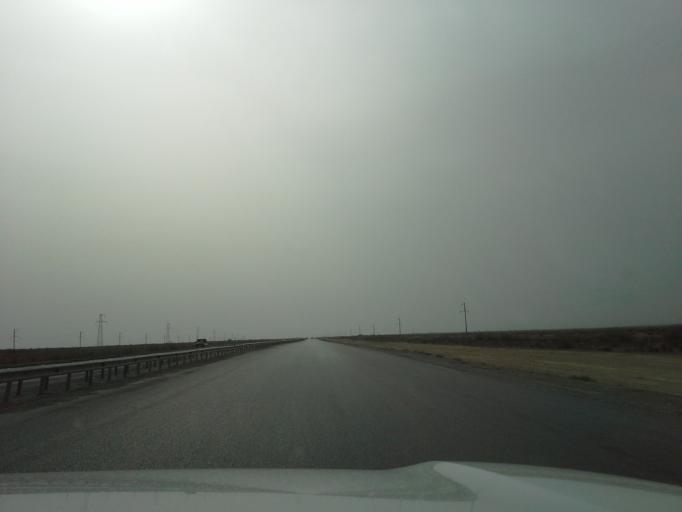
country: TM
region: Ahal
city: Kaka
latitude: 37.5101
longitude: 59.4425
